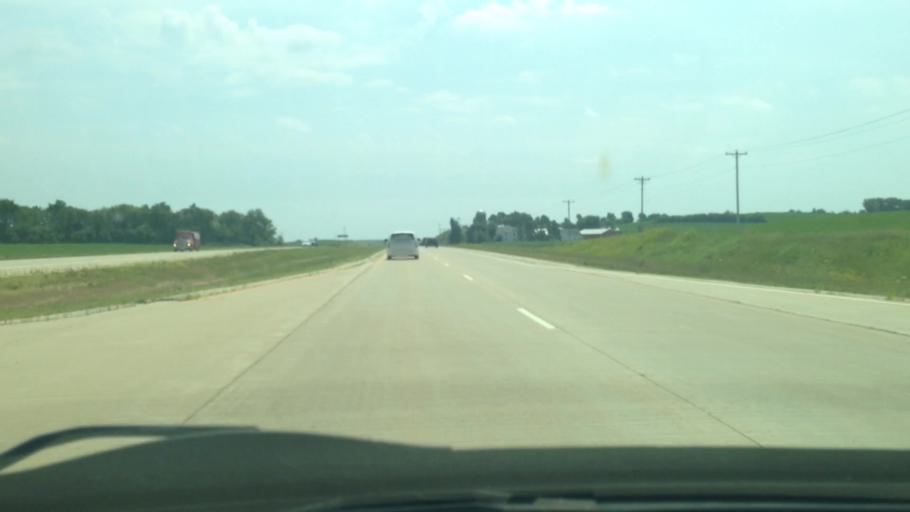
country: US
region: Wisconsin
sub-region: Dane County
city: Waunakee
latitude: 43.1829
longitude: -89.5505
